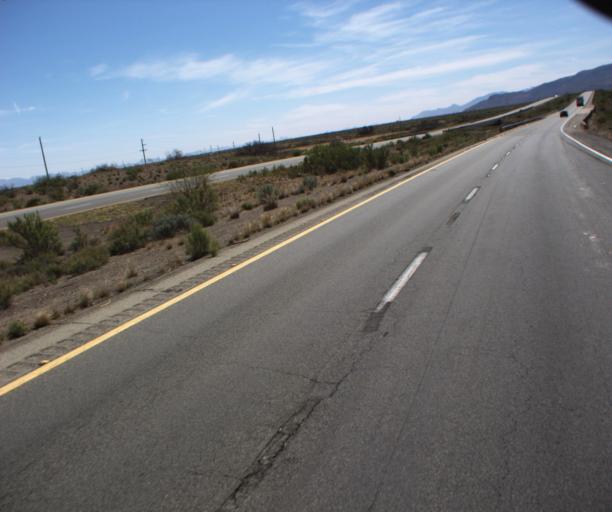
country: US
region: Arizona
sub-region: Cochise County
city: Willcox
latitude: 32.3586
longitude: -109.6141
